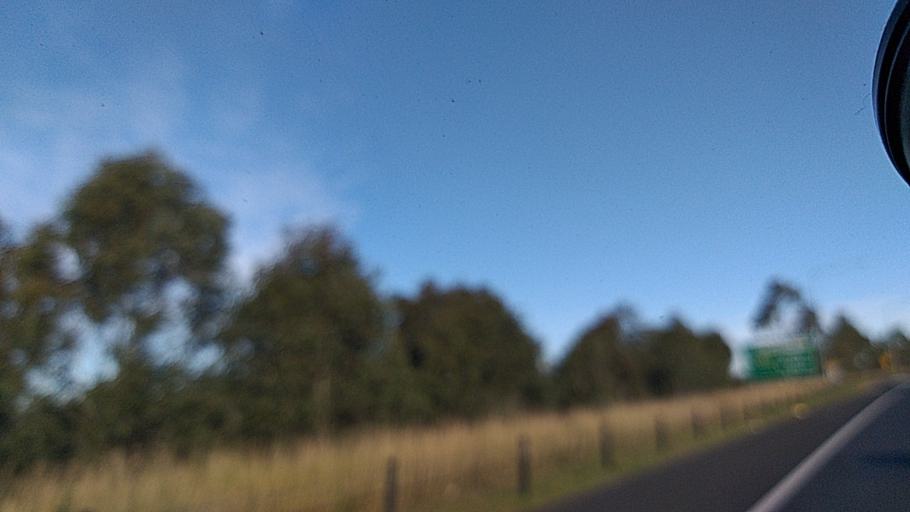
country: AU
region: New South Wales
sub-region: Blacktown
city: Doonside
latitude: -33.7828
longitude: 150.8584
